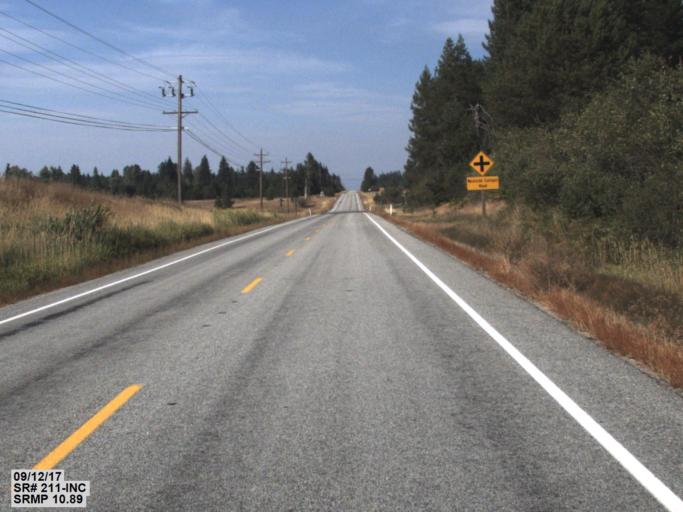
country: US
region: Washington
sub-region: Pend Oreille County
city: Newport
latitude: 48.2429
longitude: -117.2844
